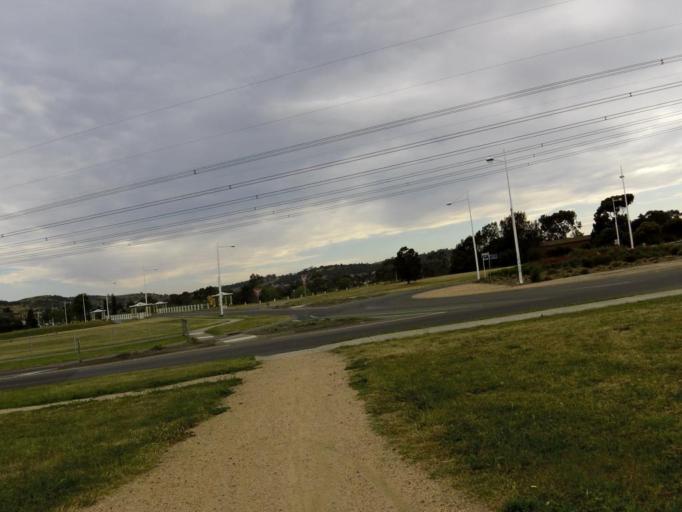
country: AU
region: Victoria
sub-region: Whittlesea
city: Mill Park
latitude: -37.6425
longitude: 145.0688
